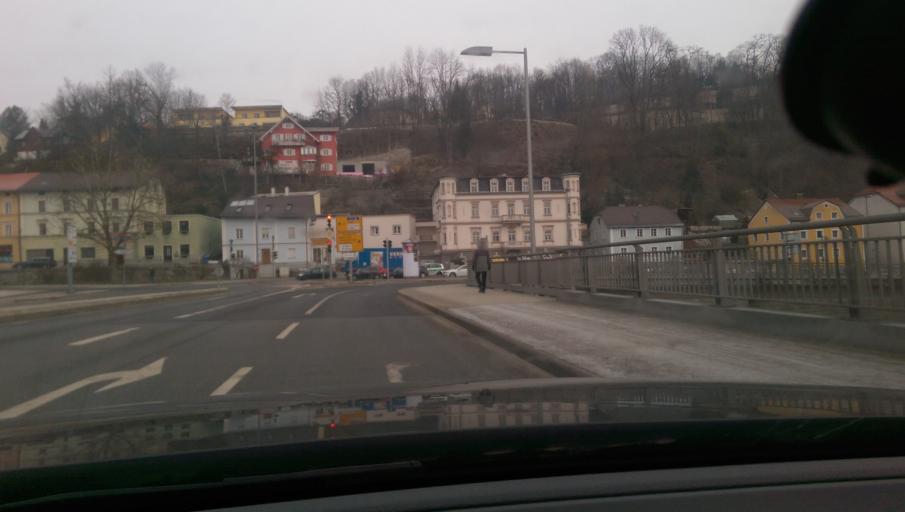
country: DE
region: Bavaria
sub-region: Lower Bavaria
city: Passau
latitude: 48.5766
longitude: 13.4555
